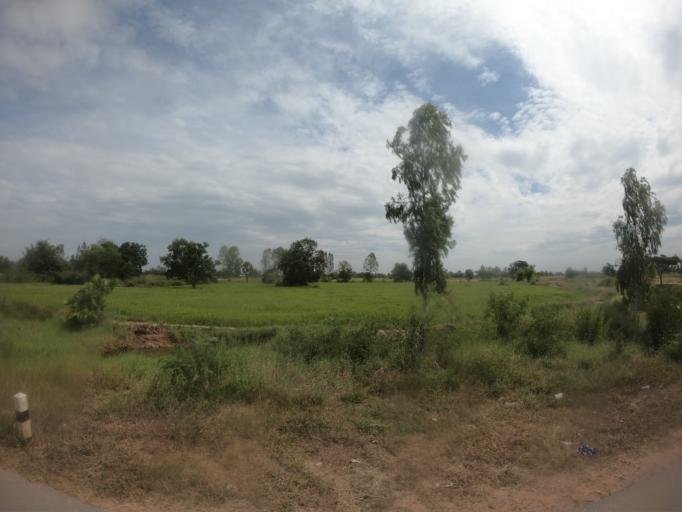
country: TH
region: Maha Sarakham
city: Chiang Yuen
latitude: 16.3823
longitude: 103.1034
